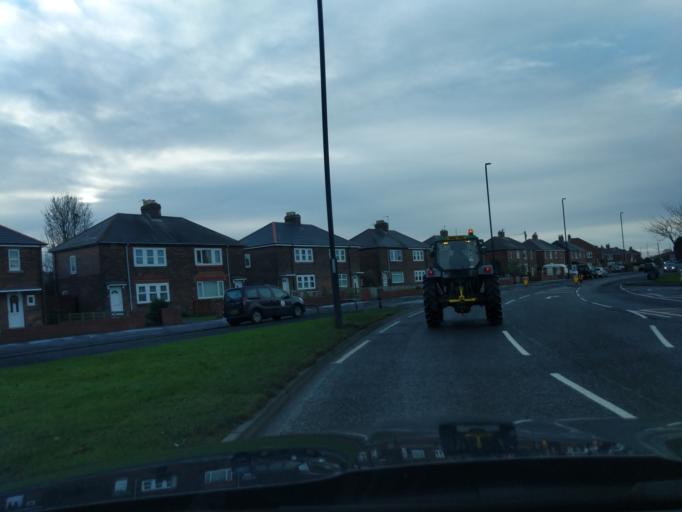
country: GB
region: England
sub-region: South Tyneside
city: Jarrow
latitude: 54.9989
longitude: -1.4882
